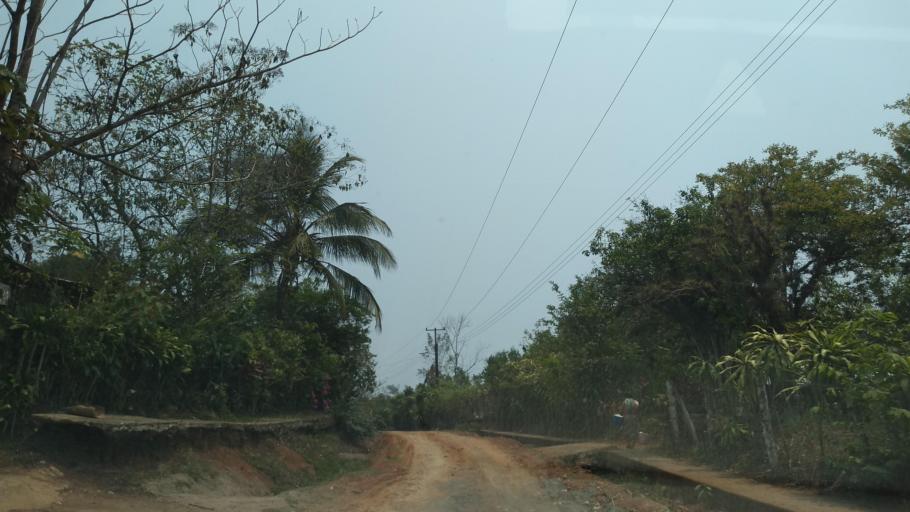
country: MX
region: Puebla
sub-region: San Sebastian Tlacotepec
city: San Martin Mazateopan
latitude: 18.4940
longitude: -96.7798
